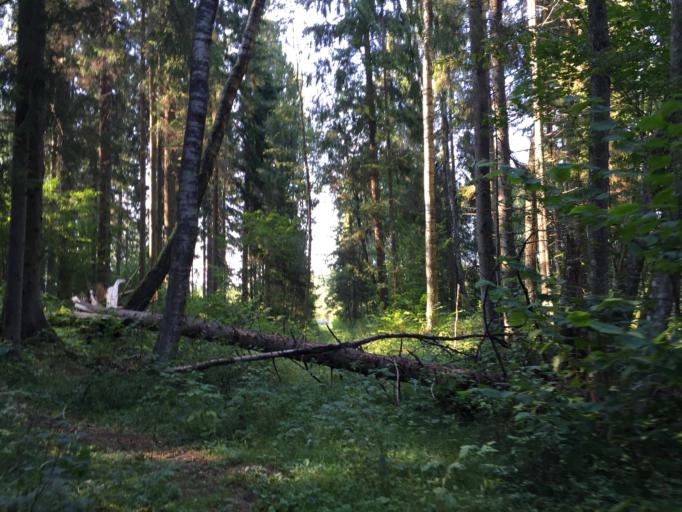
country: LV
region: Limbazu Rajons
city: Limbazi
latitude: 57.5662
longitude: 24.8002
